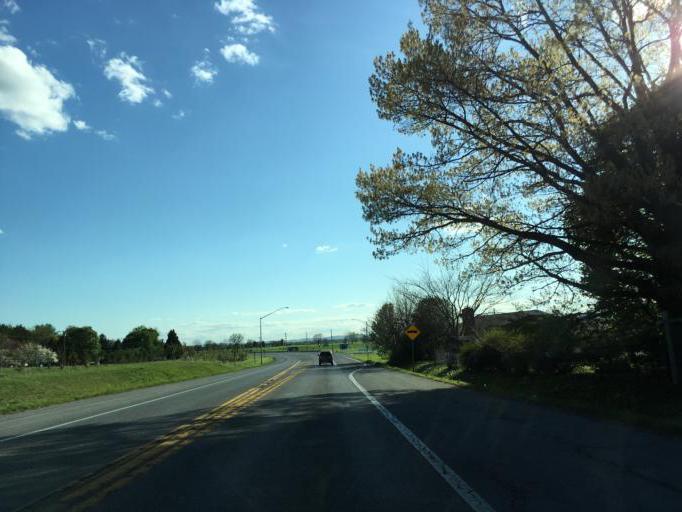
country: US
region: Maryland
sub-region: Frederick County
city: Walkersville
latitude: 39.4756
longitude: -77.3570
